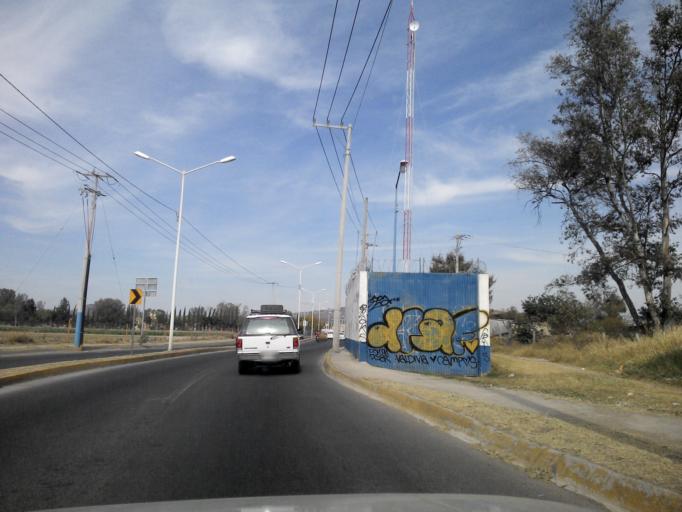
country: MX
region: Jalisco
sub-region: San Pedro Tlaquepaque
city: Paseo del Prado
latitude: 20.5595
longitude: -103.3940
